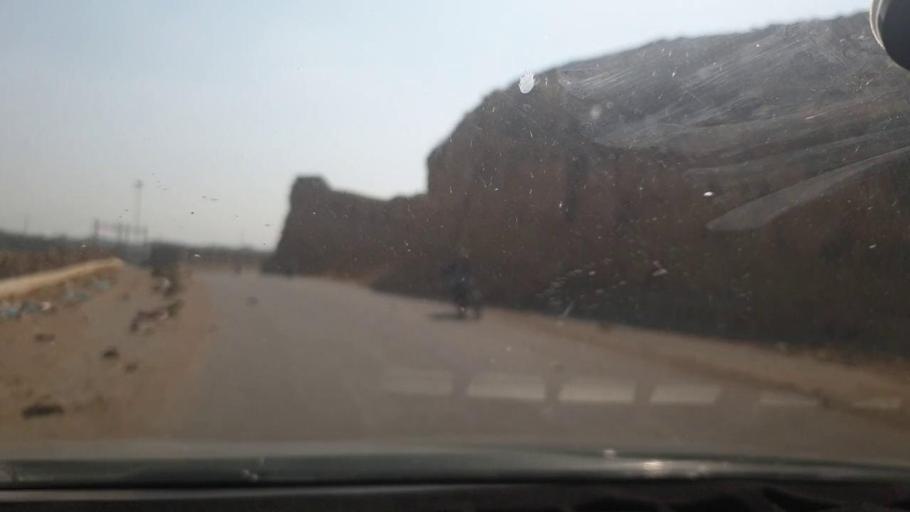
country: PK
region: Sindh
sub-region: Karachi District
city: Karachi
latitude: 24.9717
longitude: 66.9977
